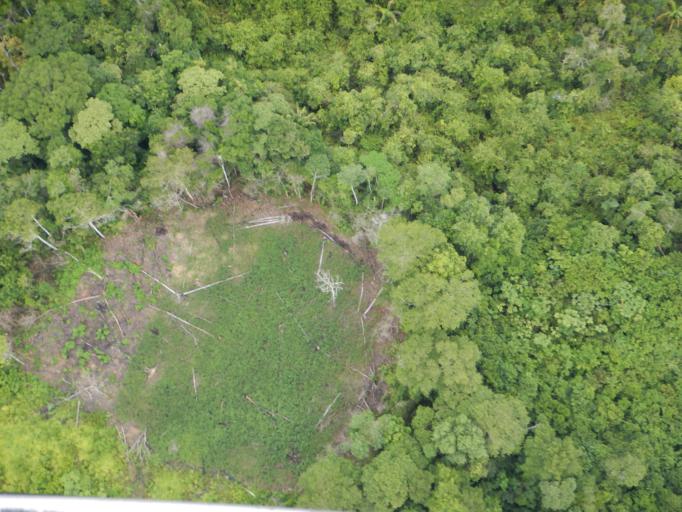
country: BO
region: Cochabamba
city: Chimore
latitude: -16.9024
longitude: -64.8890
